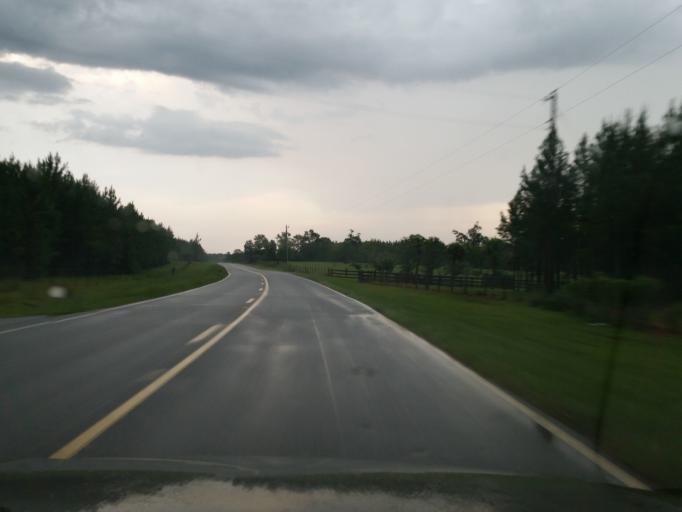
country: US
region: Florida
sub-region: Escambia County
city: Cantonment
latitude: 30.6138
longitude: -87.4176
